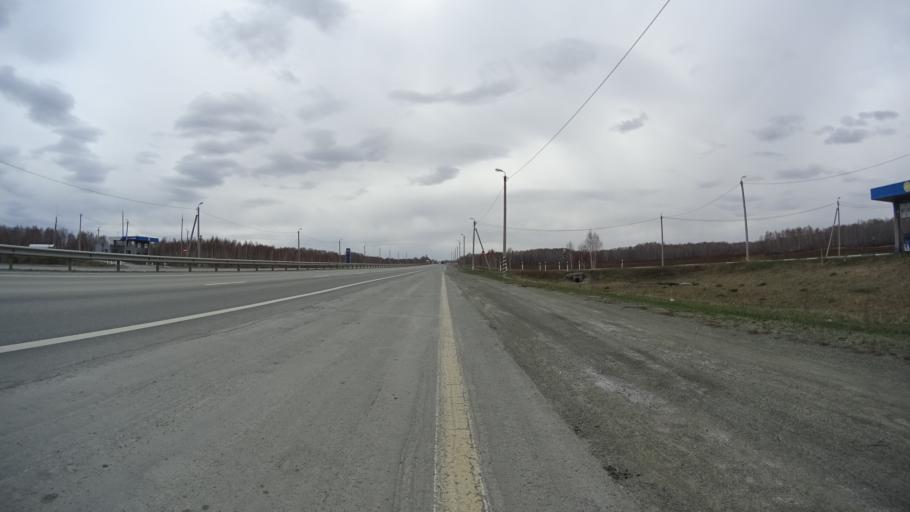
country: RU
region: Chelyabinsk
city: Yemanzhelinka
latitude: 54.8341
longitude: 61.3123
